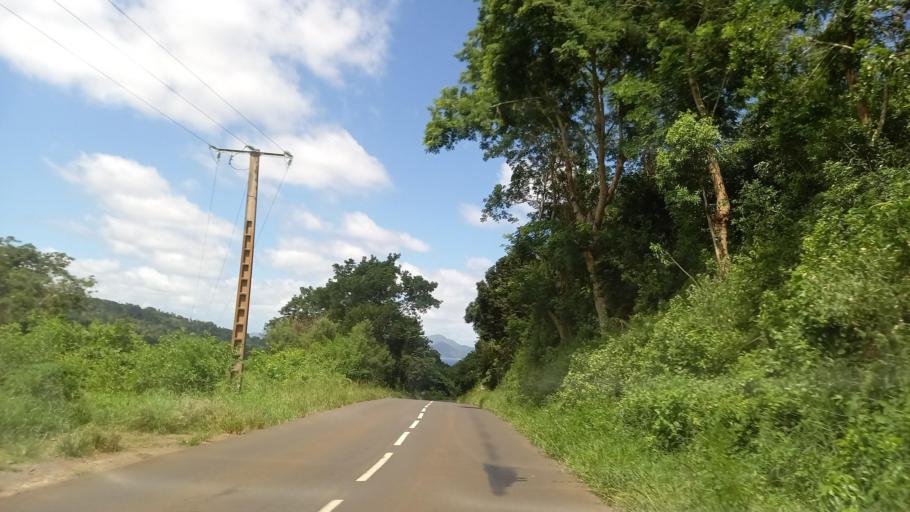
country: YT
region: Acoua
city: Acoua
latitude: -12.7446
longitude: 45.0545
